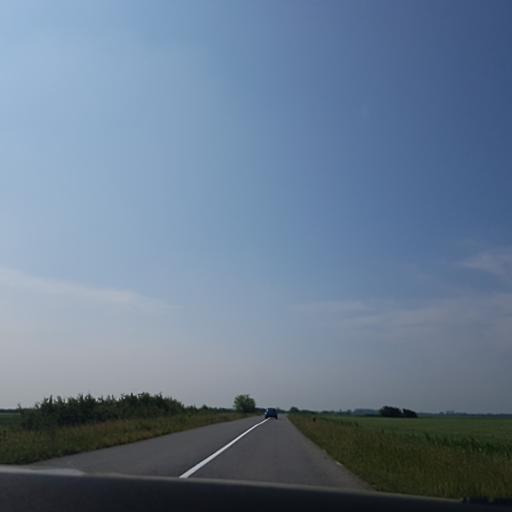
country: RS
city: Jarkovac
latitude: 45.2948
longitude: 20.7640
